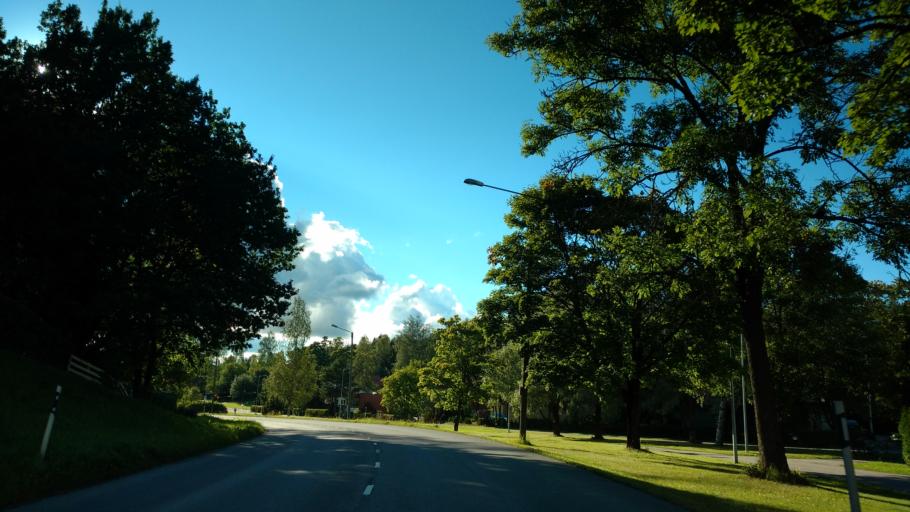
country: FI
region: Varsinais-Suomi
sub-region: Salo
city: Halikko
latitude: 60.3966
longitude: 23.0999
